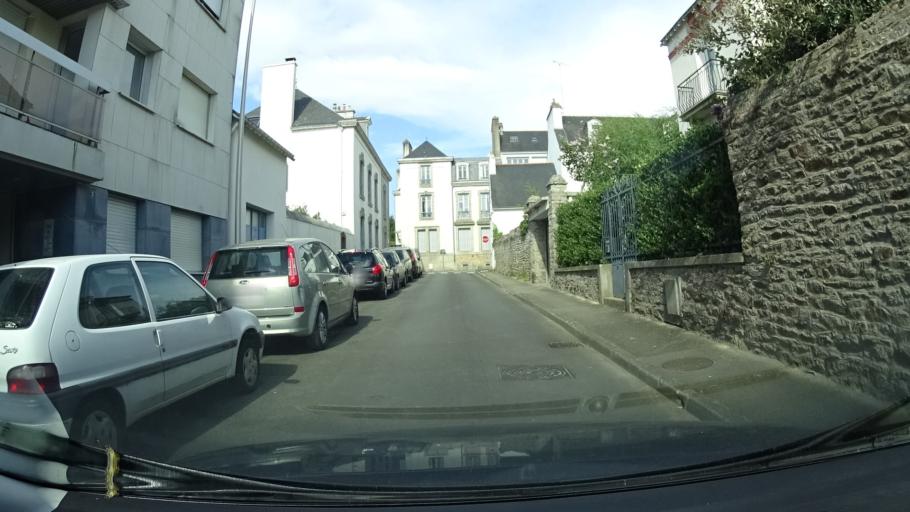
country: FR
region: Brittany
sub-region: Departement du Morbihan
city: Vannes
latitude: 47.6545
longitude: -2.7653
